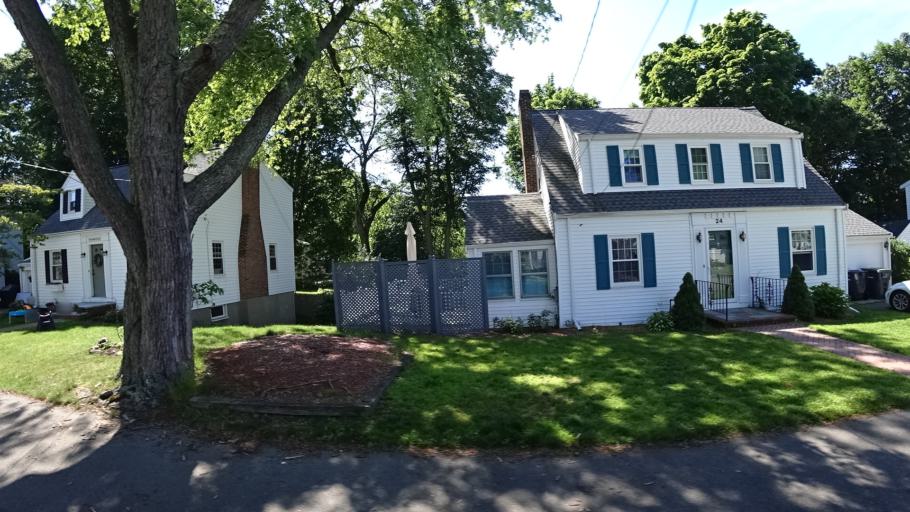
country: US
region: Massachusetts
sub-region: Norfolk County
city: Dedham
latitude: 42.2413
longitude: -71.1672
